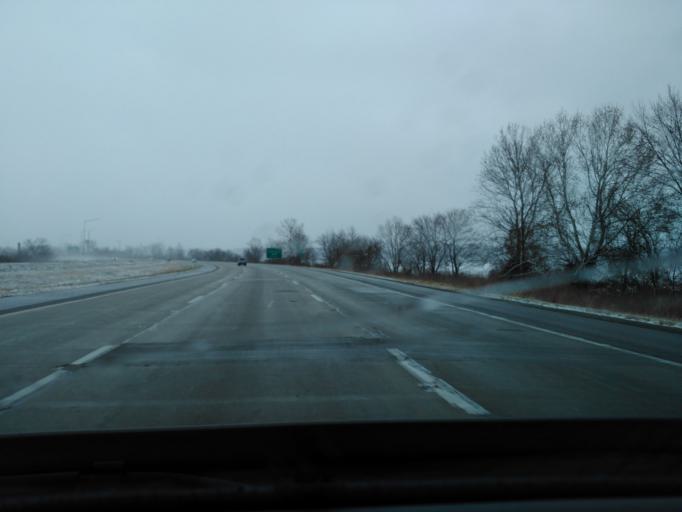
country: US
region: Illinois
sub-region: Saint Clair County
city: Caseyville
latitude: 38.6509
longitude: -90.0360
